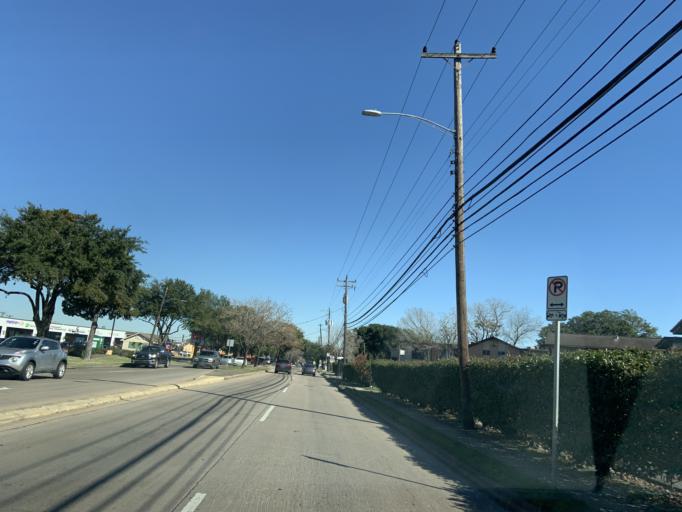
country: US
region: Texas
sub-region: Harris County
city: Bellaire
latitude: 29.6875
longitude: -95.5072
